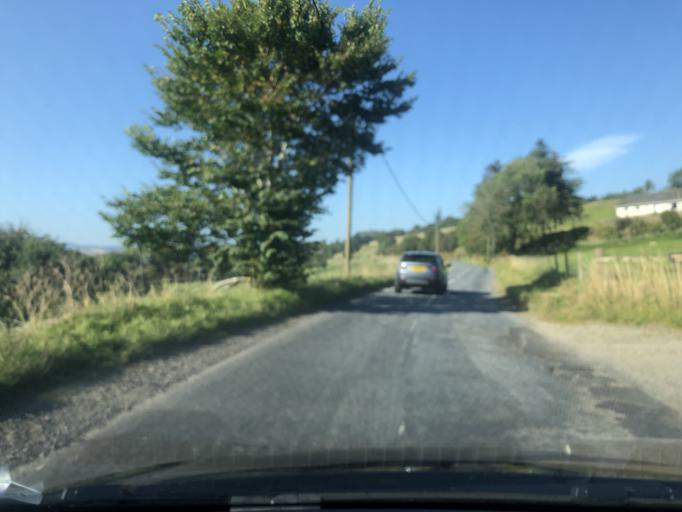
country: GB
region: Scotland
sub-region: Perth and Kinross
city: Blairgowrie
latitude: 56.6688
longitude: -3.4564
